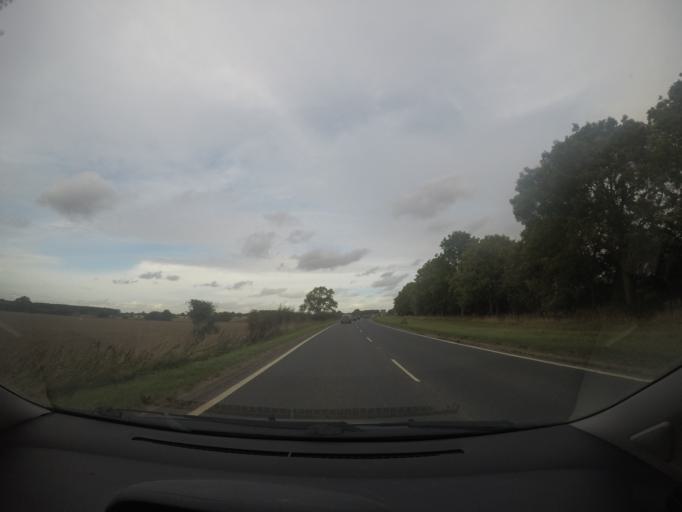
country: GB
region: England
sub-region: North Yorkshire
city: Riccall
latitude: 53.8614
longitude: -1.0509
